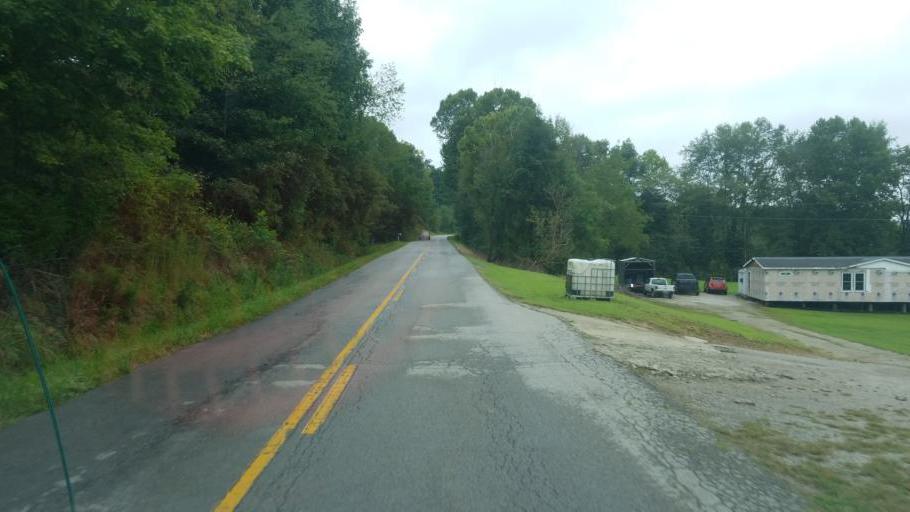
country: US
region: Kentucky
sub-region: Rowan County
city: Morehead
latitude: 38.3587
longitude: -83.5331
